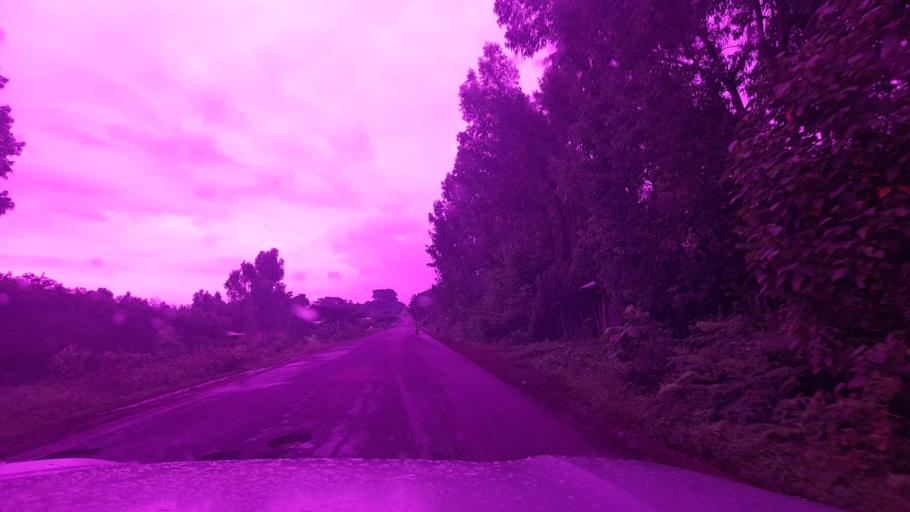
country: ET
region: Oromiya
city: Jima
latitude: 7.7248
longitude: 37.2589
